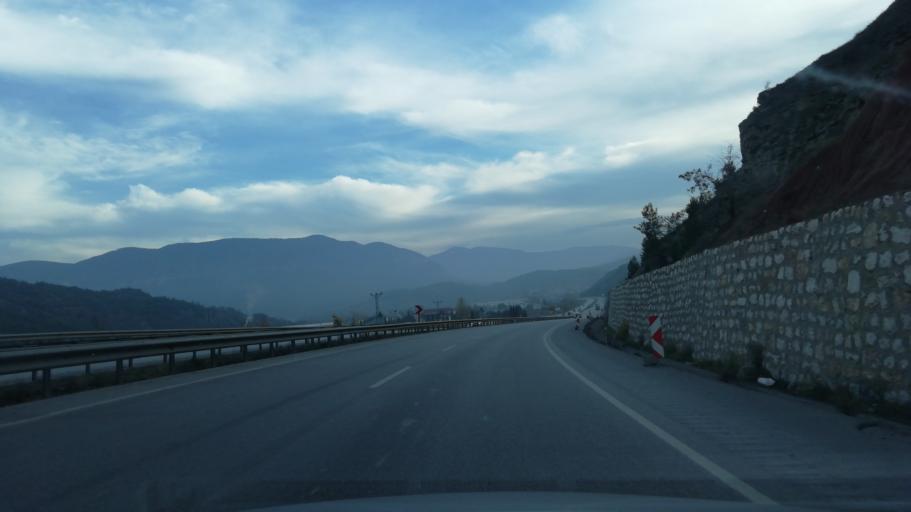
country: TR
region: Karabuk
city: Karabuk
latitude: 41.1481
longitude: 32.6667
